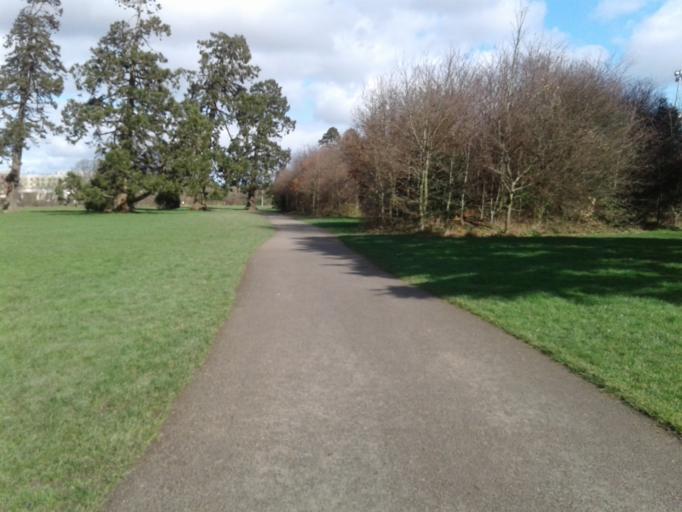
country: IE
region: Leinster
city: Beaumont
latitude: 53.4009
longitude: -6.2469
